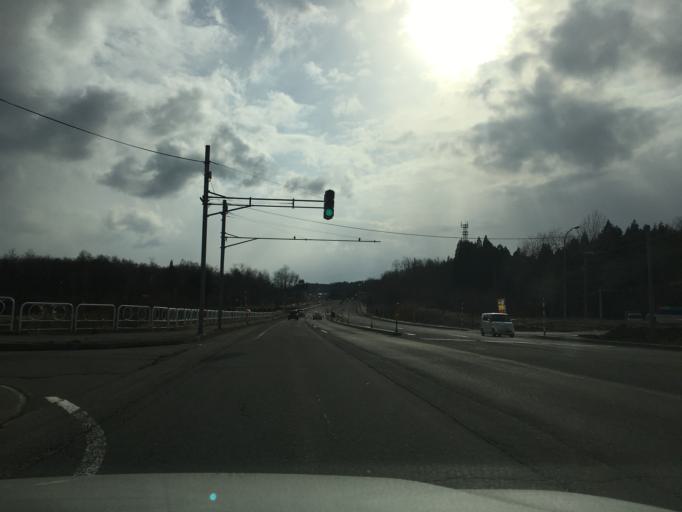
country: JP
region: Aomori
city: Aomori Shi
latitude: 40.8284
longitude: 140.6587
